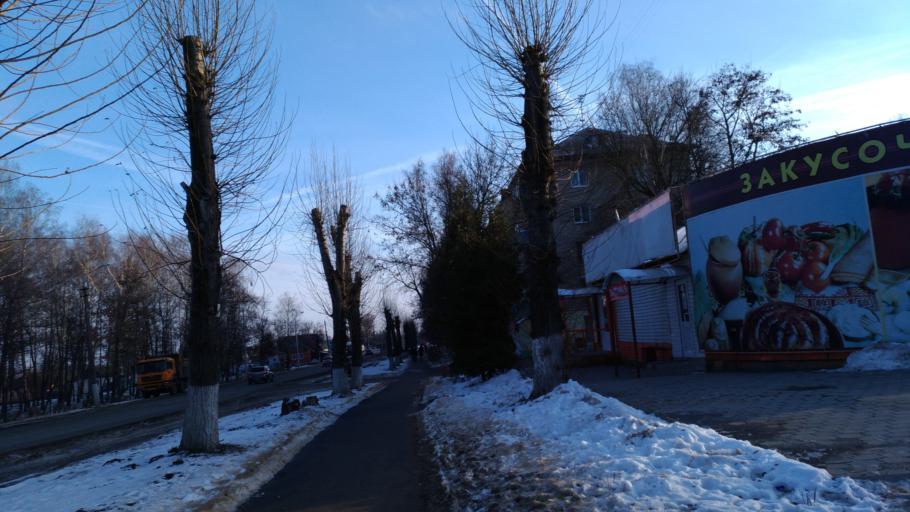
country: RU
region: Tula
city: Tula
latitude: 54.1925
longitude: 37.6944
